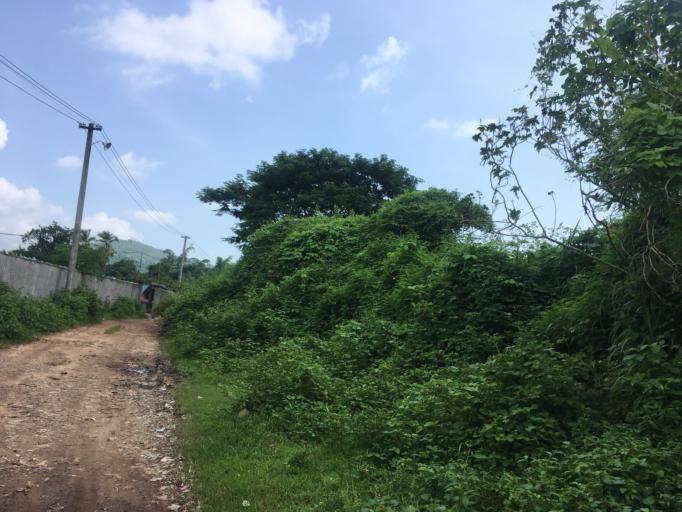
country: MM
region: Mon
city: Mawlamyine
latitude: 16.4587
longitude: 97.6654
